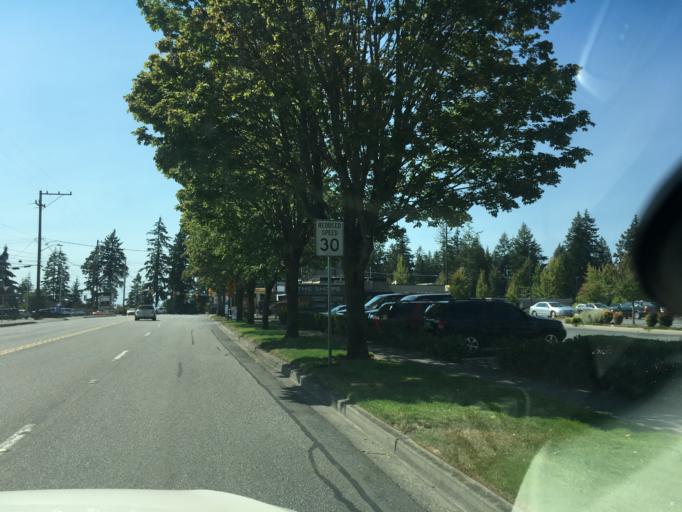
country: US
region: Washington
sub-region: King County
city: Shoreline
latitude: 47.7651
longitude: -122.3642
